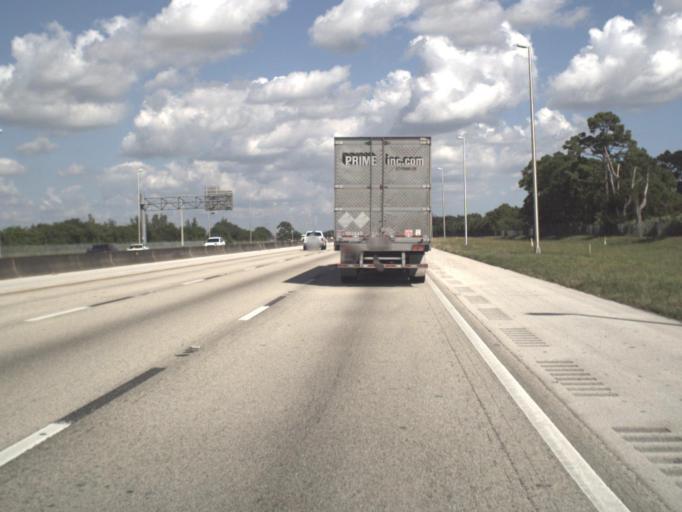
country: US
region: Florida
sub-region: Palm Beach County
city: Villages of Oriole
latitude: 26.4754
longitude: -80.1736
